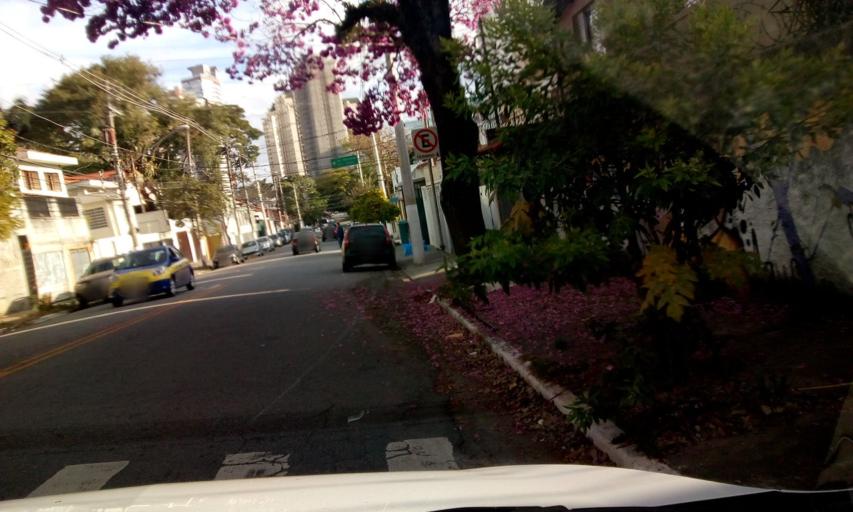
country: BR
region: Sao Paulo
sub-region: Sao Paulo
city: Sao Paulo
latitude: -23.6163
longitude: -46.6933
